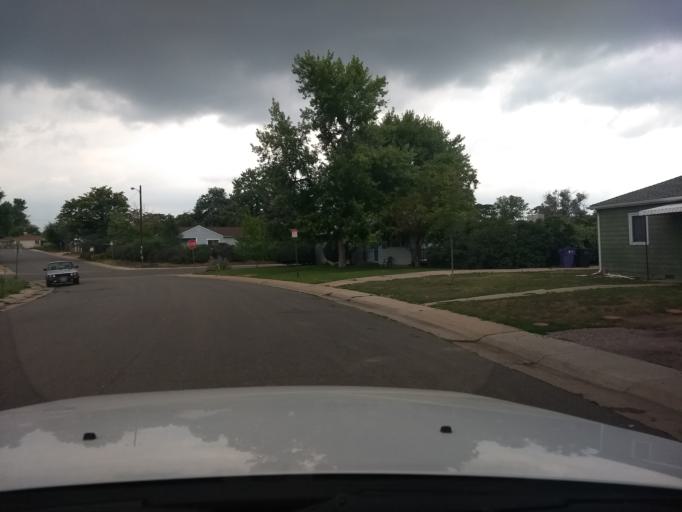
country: US
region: Colorado
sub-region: Denver County
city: Denver
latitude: 39.7062
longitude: -105.0092
